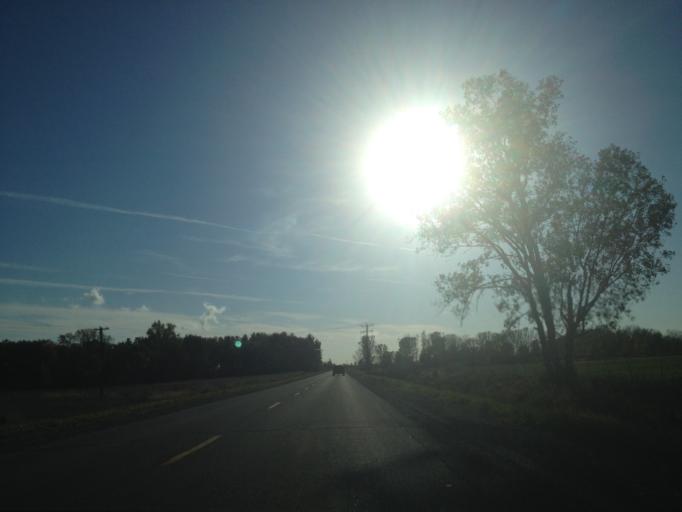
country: CA
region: Ontario
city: Delaware
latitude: 42.6407
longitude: -81.5556
